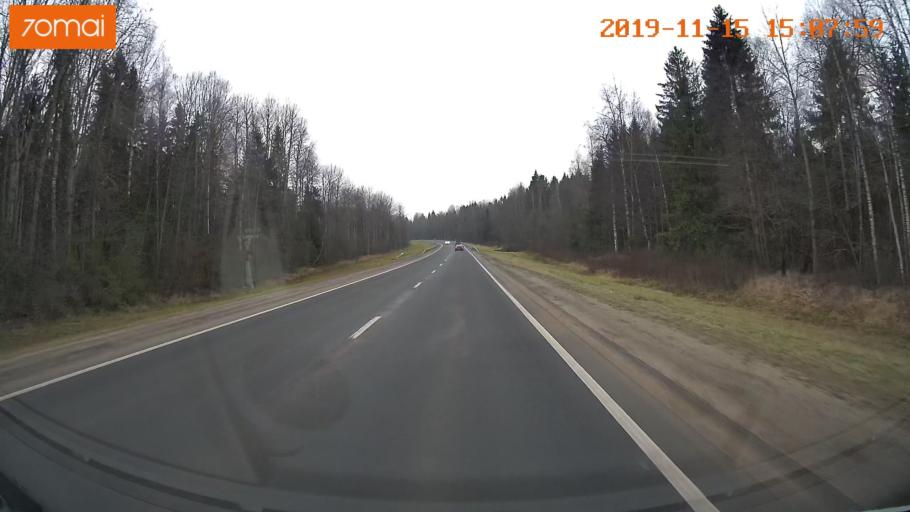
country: RU
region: Jaroslavl
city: Prechistoye
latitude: 58.3769
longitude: 40.2840
